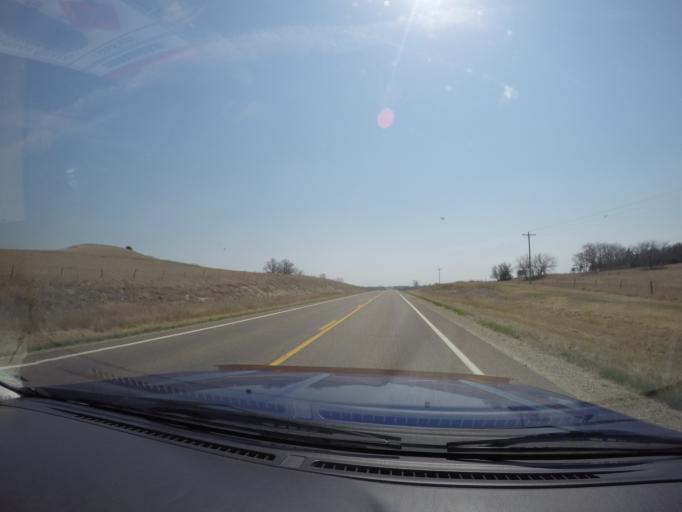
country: US
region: Kansas
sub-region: Morris County
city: Council Grove
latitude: 38.7153
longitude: -96.4975
